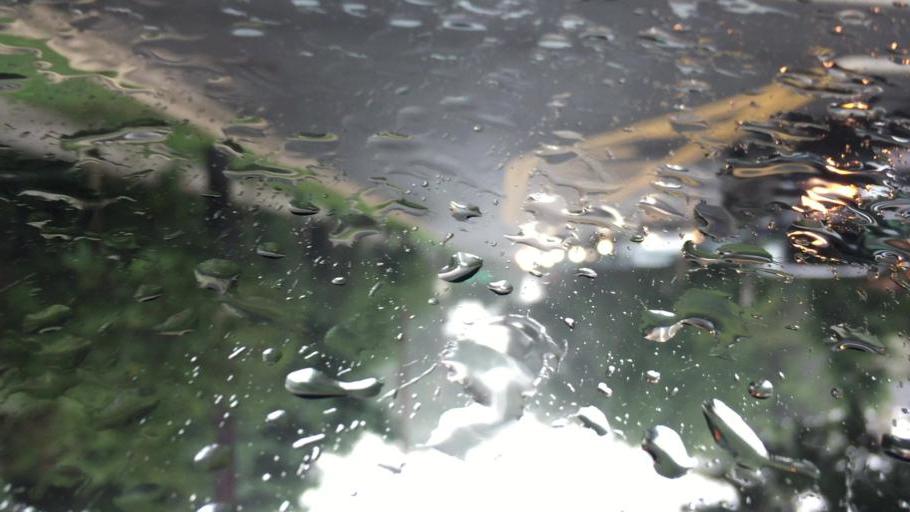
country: US
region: Maryland
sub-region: Montgomery County
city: Friendship Village
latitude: 38.9314
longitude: -77.0664
